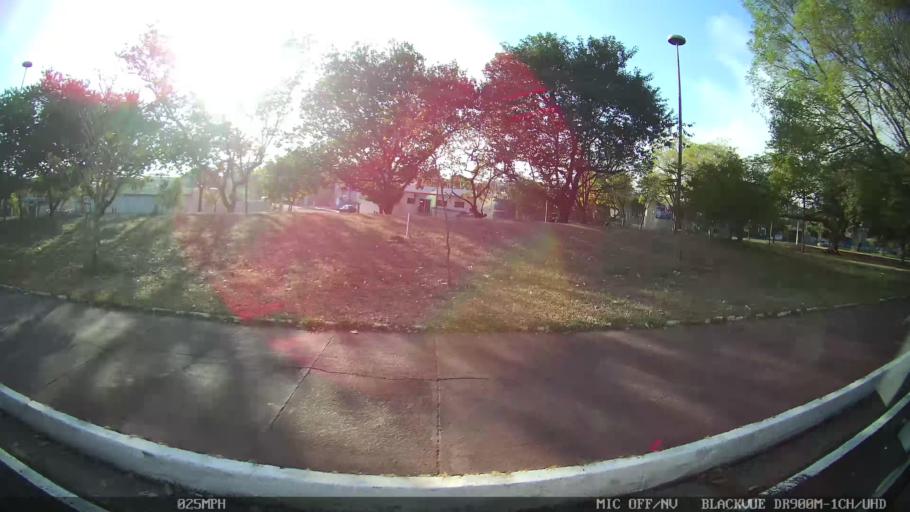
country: BR
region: Sao Paulo
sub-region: Sao Jose Do Rio Preto
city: Sao Jose do Rio Preto
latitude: -20.8309
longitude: -49.3662
